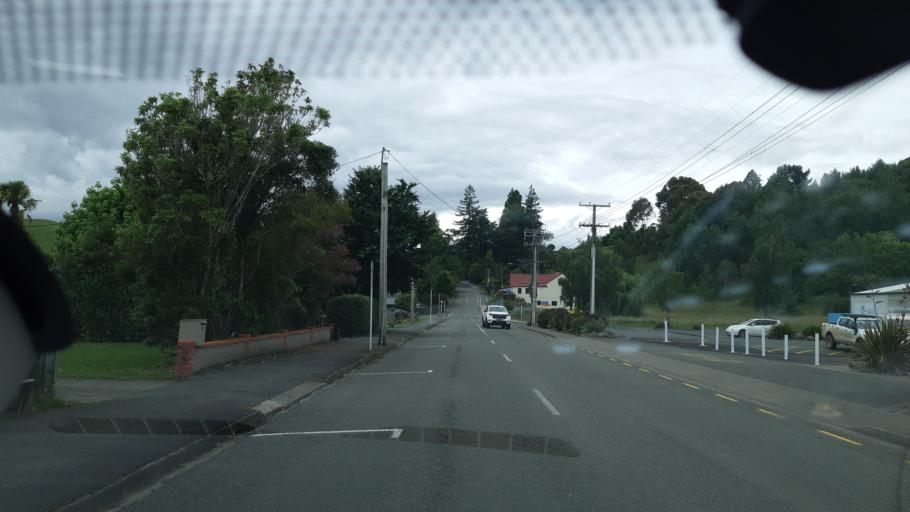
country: NZ
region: Tasman
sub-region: Tasman District
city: Wakefield
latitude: -41.4076
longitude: 173.0447
